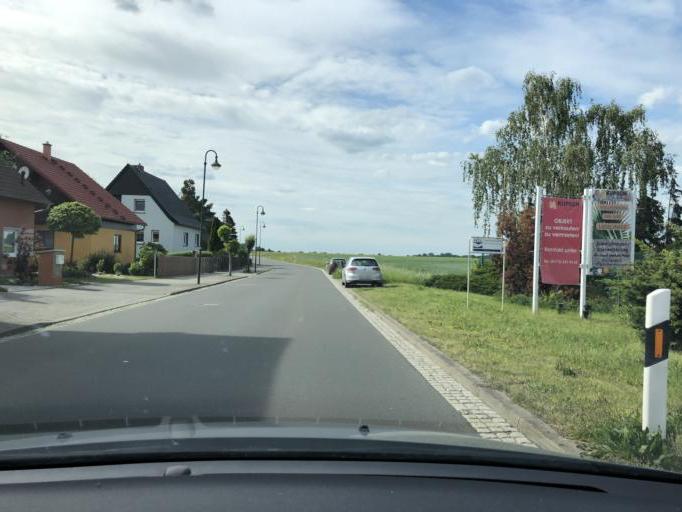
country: DE
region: Saxony
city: Nerchau
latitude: 51.2754
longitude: 12.7858
